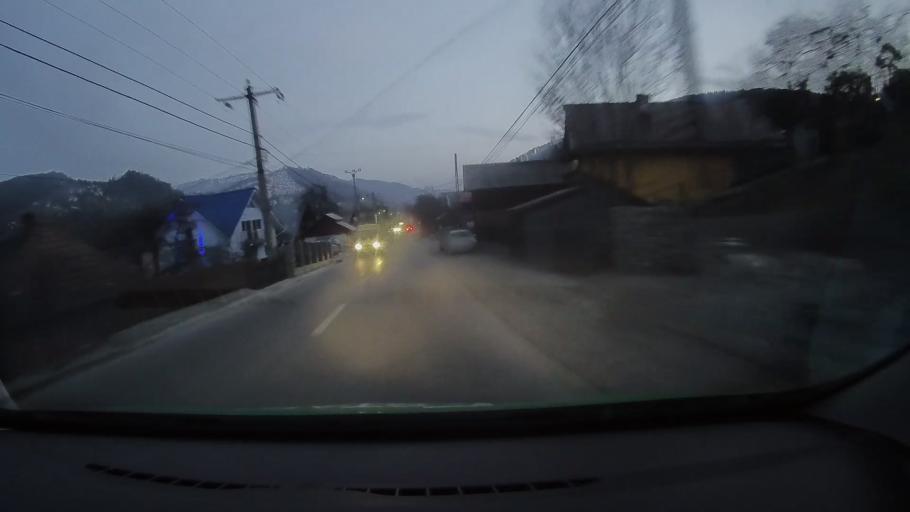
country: RO
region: Prahova
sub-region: Comuna Valea Doftanei
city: Tesila
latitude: 45.2952
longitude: 25.7208
